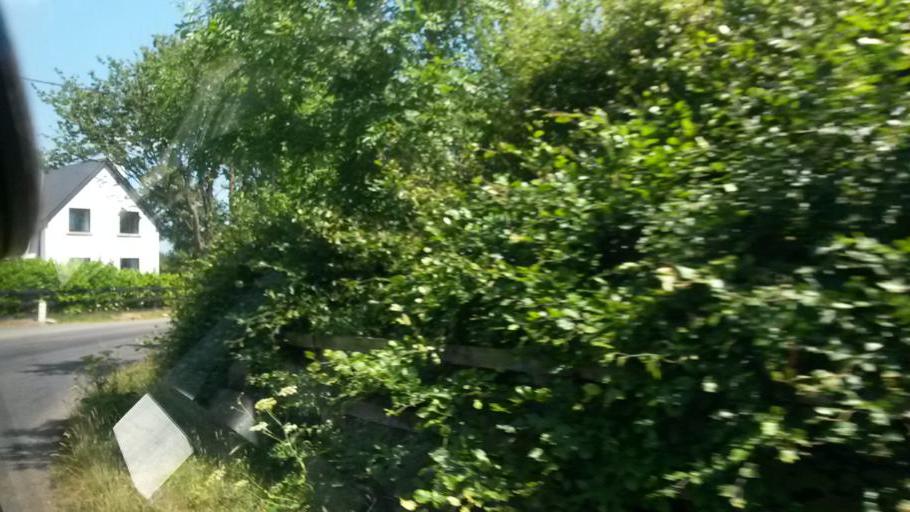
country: IE
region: Leinster
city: Balrothery
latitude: 53.5405
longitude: -6.2456
